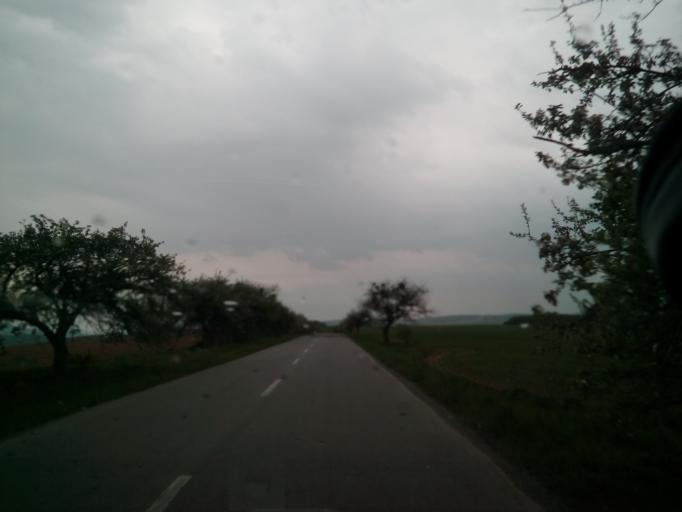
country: SK
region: Kosicky
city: Secovce
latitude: 48.7709
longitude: 21.4734
